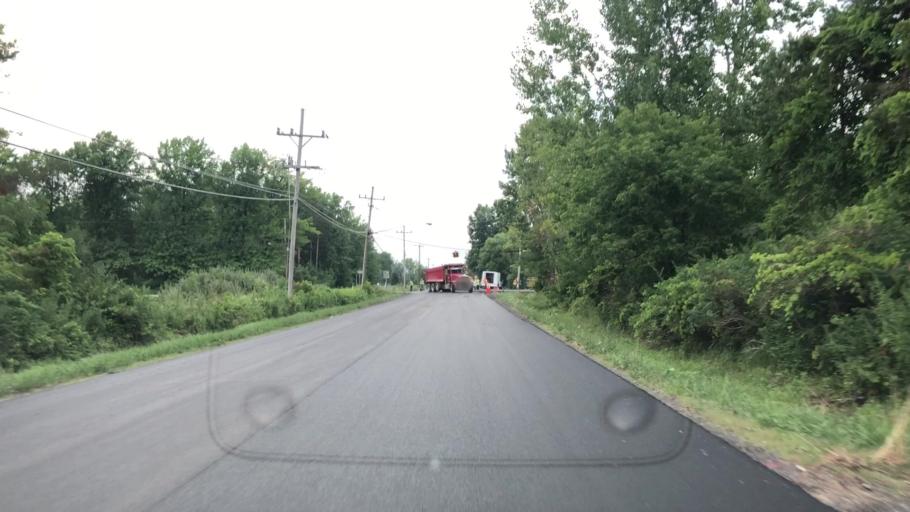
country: US
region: New York
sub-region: Erie County
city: Elma Center
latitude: 42.8215
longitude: -78.6059
